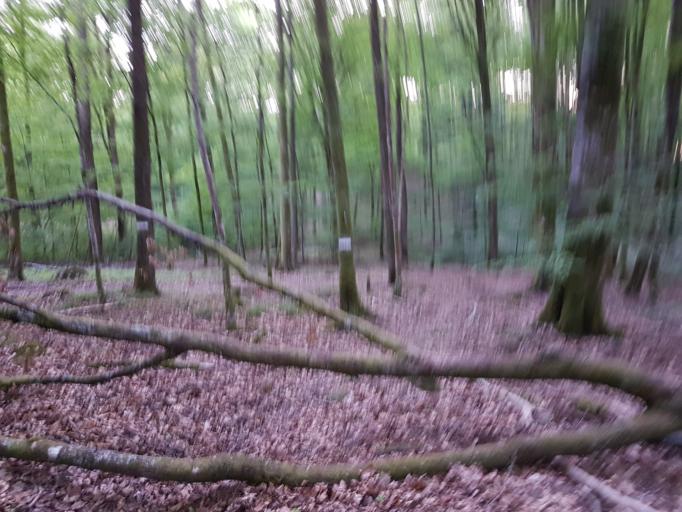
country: FR
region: Franche-Comte
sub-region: Departement de la Haute-Saone
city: Fougerolles
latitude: 47.8585
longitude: 6.4056
